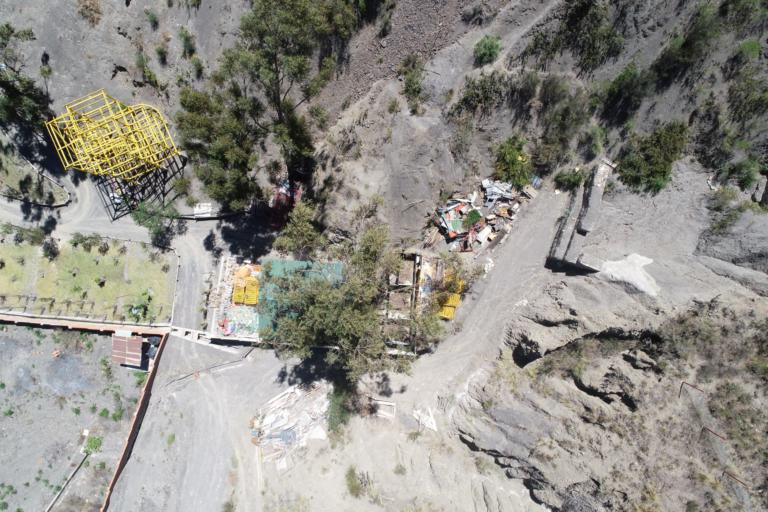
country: BO
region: La Paz
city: La Paz
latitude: -16.6246
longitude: -68.0522
